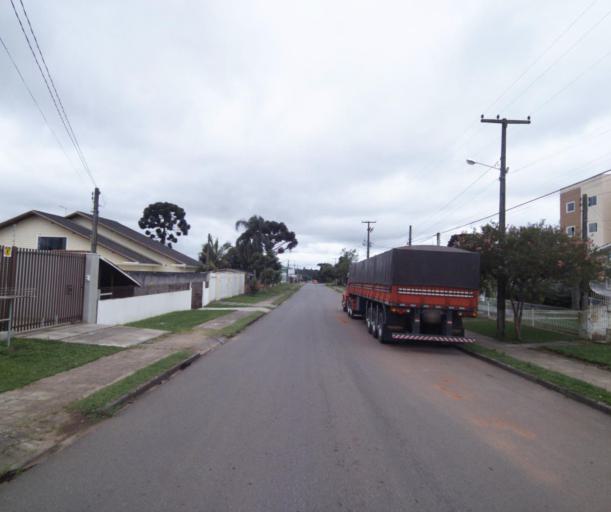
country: BR
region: Parana
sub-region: Quatro Barras
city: Quatro Barras
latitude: -25.3659
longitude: -49.1013
